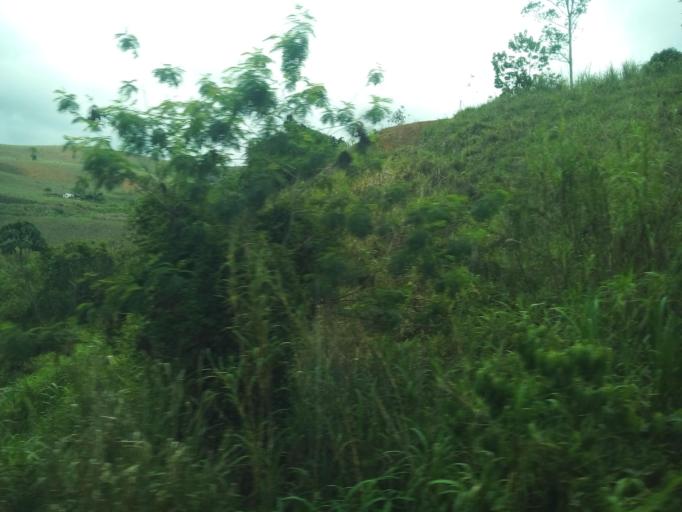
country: BR
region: Minas Gerais
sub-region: Nova Era
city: Nova Era
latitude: -19.7647
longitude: -43.0455
